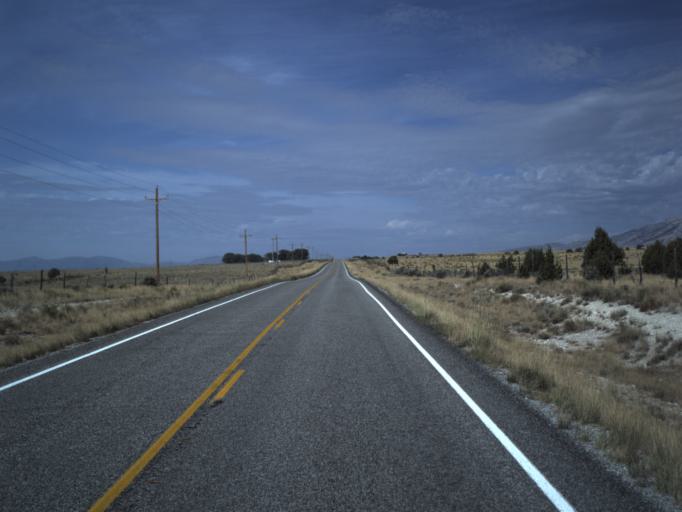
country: US
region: Idaho
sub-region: Cassia County
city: Burley
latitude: 41.8174
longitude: -113.2582
